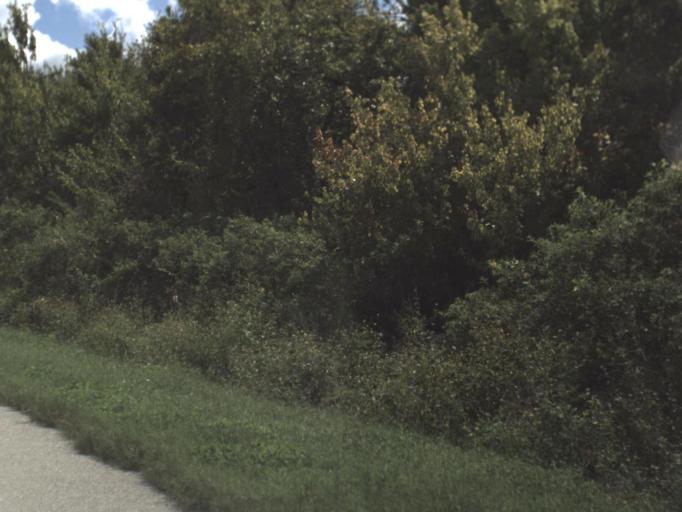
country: US
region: Florida
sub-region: DeSoto County
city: Arcadia
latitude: 27.2591
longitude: -81.9770
